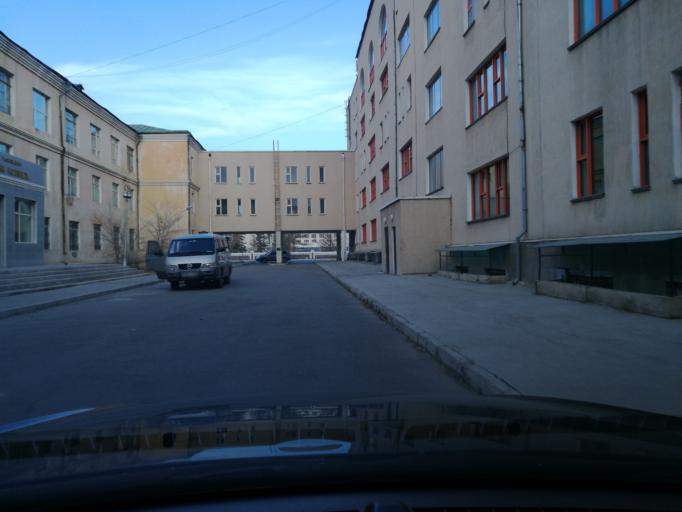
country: MN
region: Ulaanbaatar
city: Ulaanbaatar
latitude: 47.9234
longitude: 106.9259
